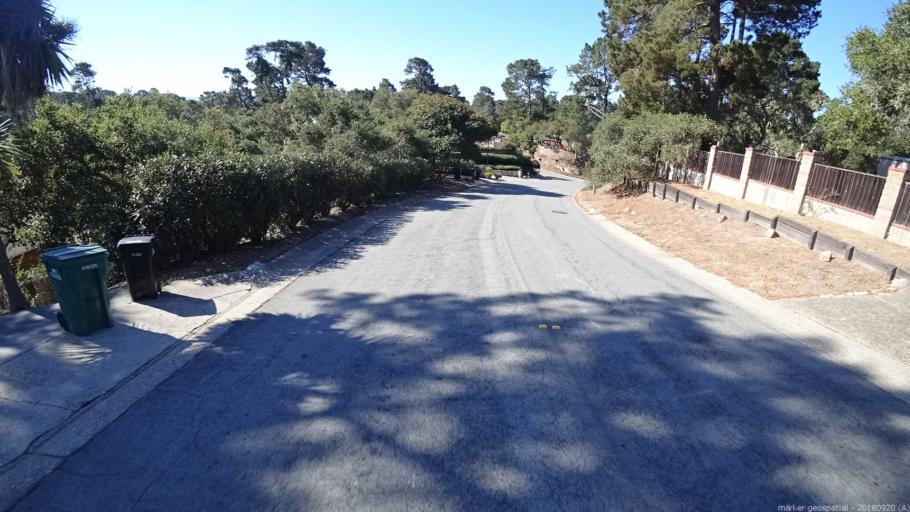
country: US
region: California
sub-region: Monterey County
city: Carmel-by-the-Sea
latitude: 36.5557
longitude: -121.8953
